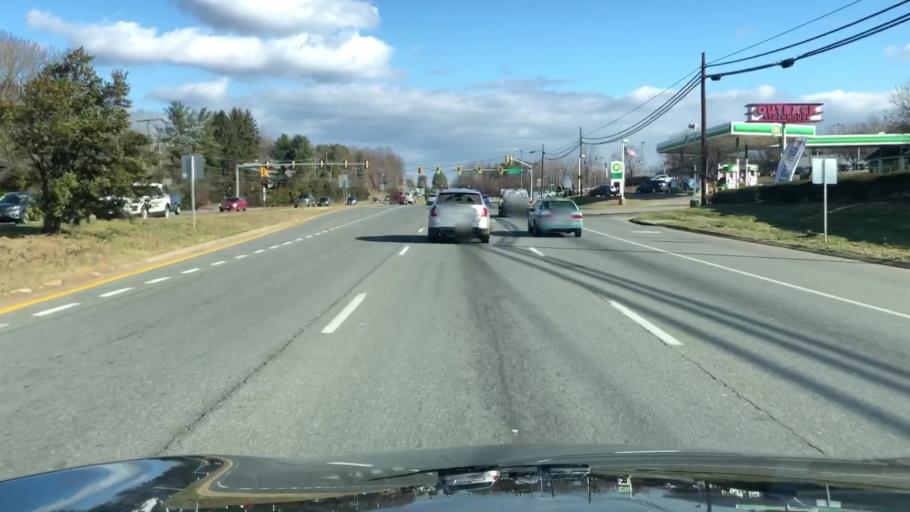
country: US
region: Virginia
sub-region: Fauquier County
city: Warrenton
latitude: 38.7338
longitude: -77.7715
